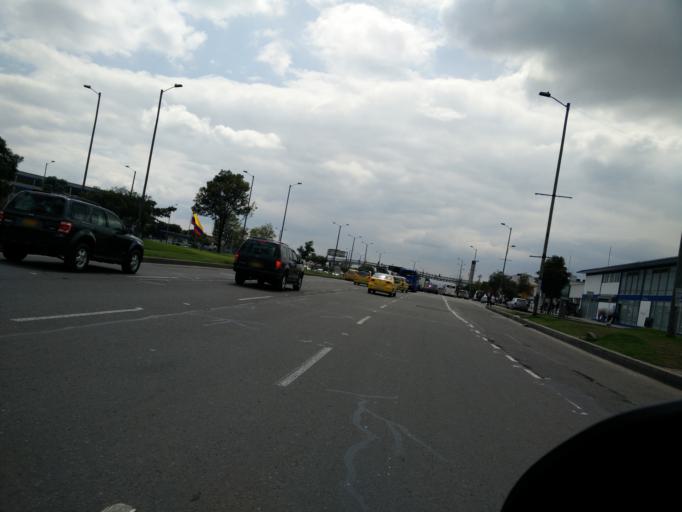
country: CO
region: Bogota D.C.
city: Bogota
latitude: 4.6279
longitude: -74.1081
